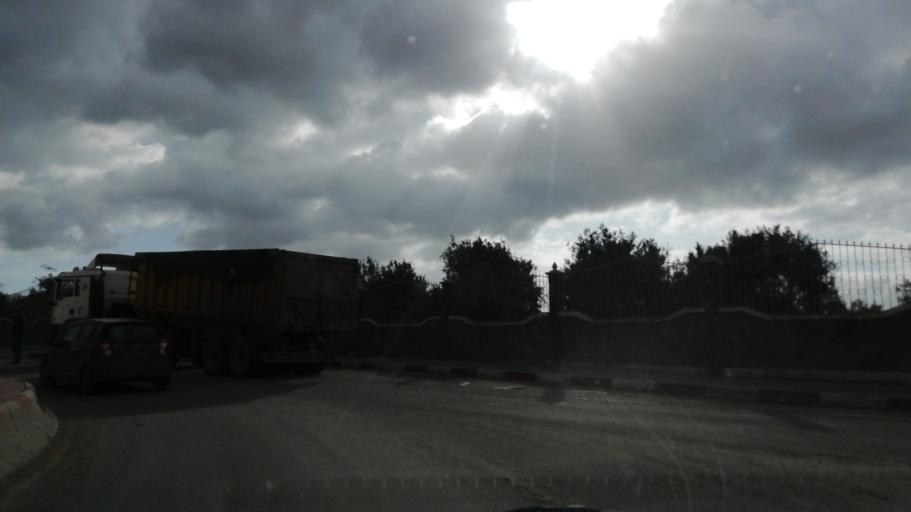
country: DZ
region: Oran
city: Sidi ech Chahmi
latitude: 35.6560
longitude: -0.5251
